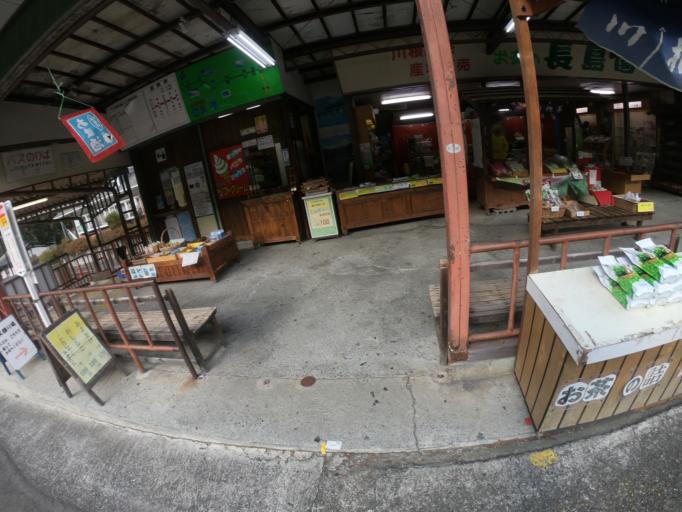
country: JP
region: Shizuoka
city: Shizuoka-shi
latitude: 35.1756
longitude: 138.1191
